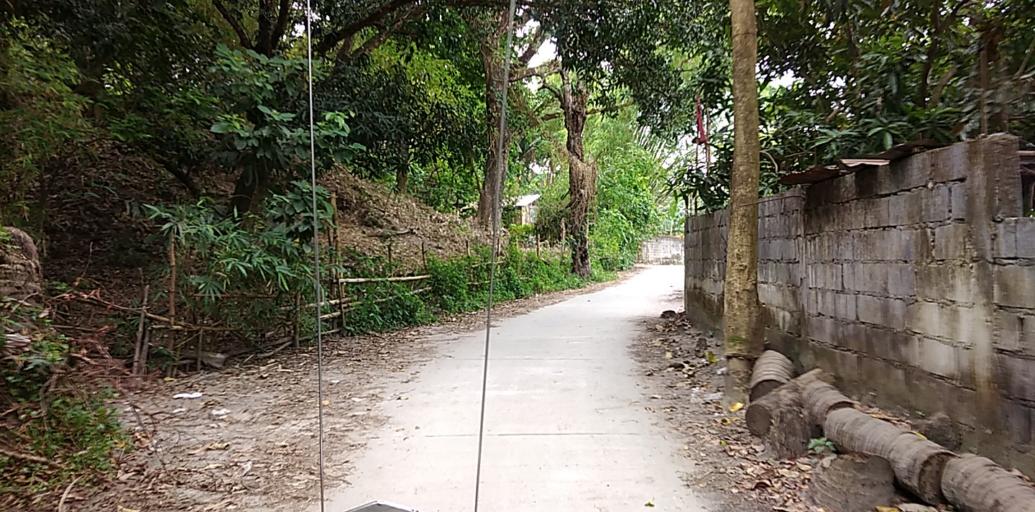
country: PH
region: Central Luzon
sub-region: Province of Pampanga
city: Porac
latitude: 15.0606
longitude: 120.5337
